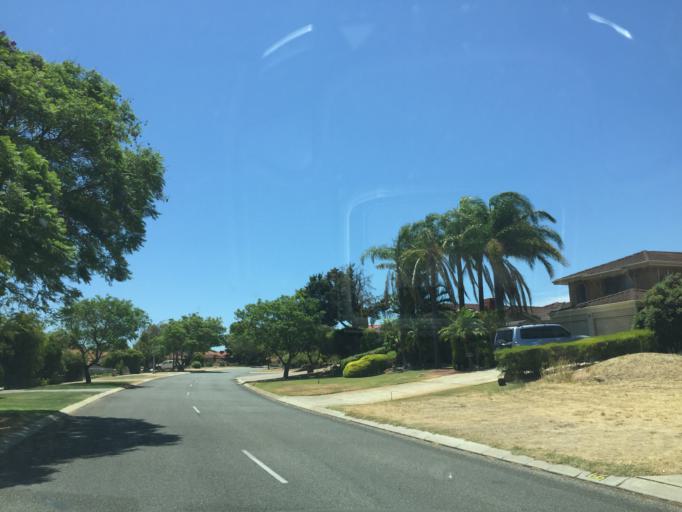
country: AU
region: Western Australia
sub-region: Melville
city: Winthrop
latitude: -32.0625
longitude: 115.8365
